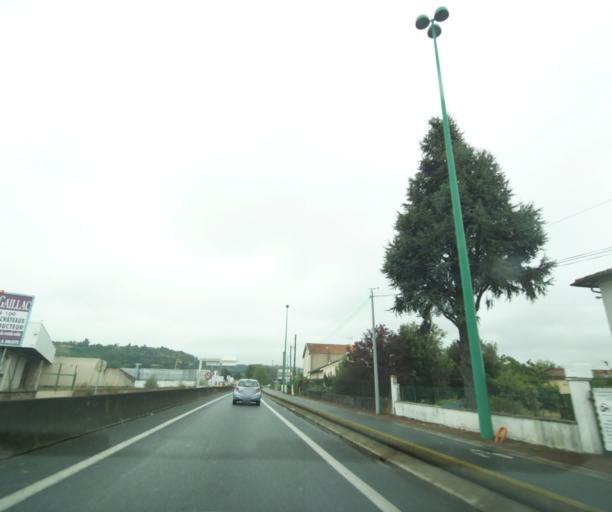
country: FR
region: Midi-Pyrenees
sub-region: Departement du Tarn
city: Albi
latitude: 43.9529
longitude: 2.1549
